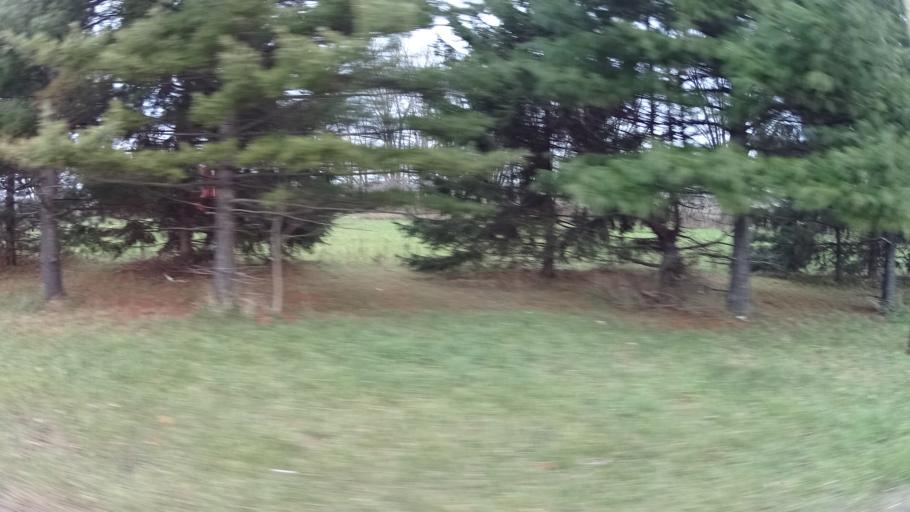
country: US
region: Ohio
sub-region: Lorain County
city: North Ridgeville
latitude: 41.4086
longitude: -82.0370
